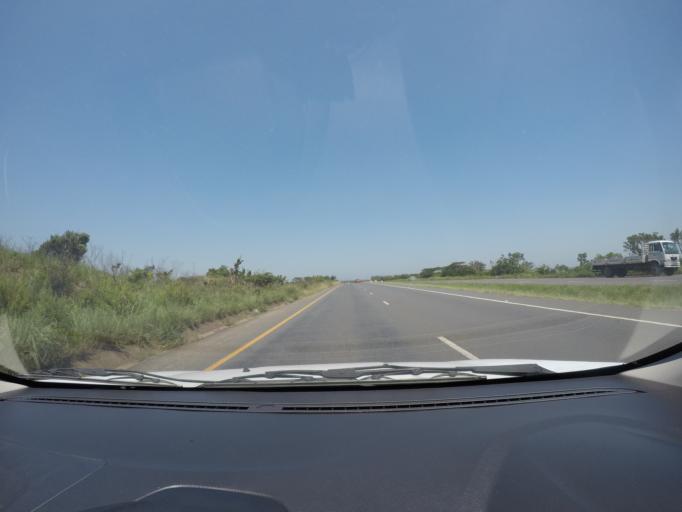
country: ZA
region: KwaZulu-Natal
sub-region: uThungulu District Municipality
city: Richards Bay
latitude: -28.7778
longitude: 31.9673
